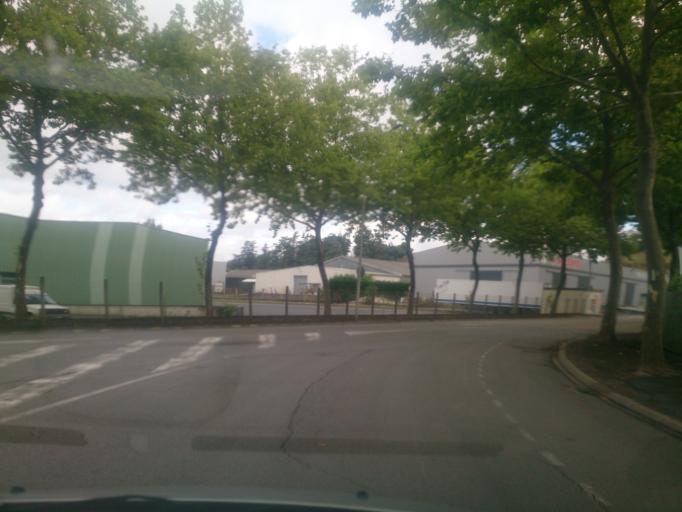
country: FR
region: Limousin
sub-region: Departement de la Correze
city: Ussac
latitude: 45.1601
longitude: 1.4870
